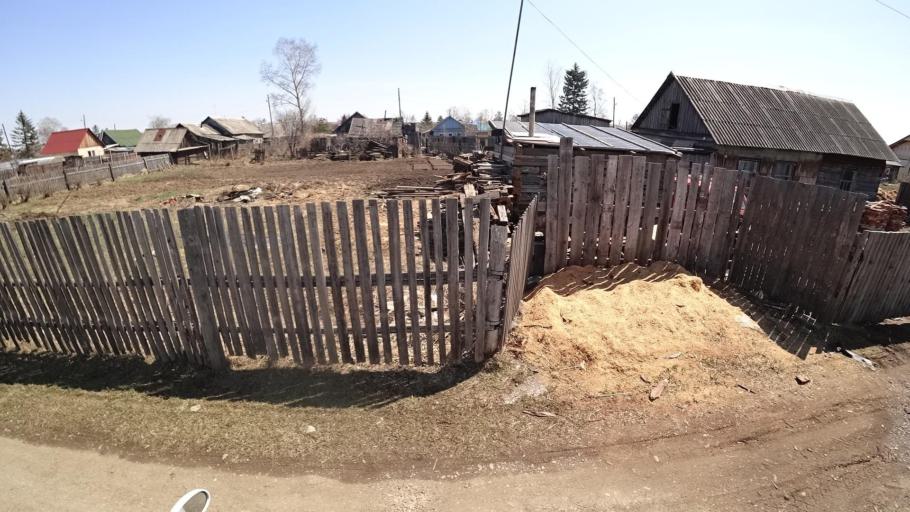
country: RU
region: Khabarovsk Krai
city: Khurba
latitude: 50.4070
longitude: 136.8844
